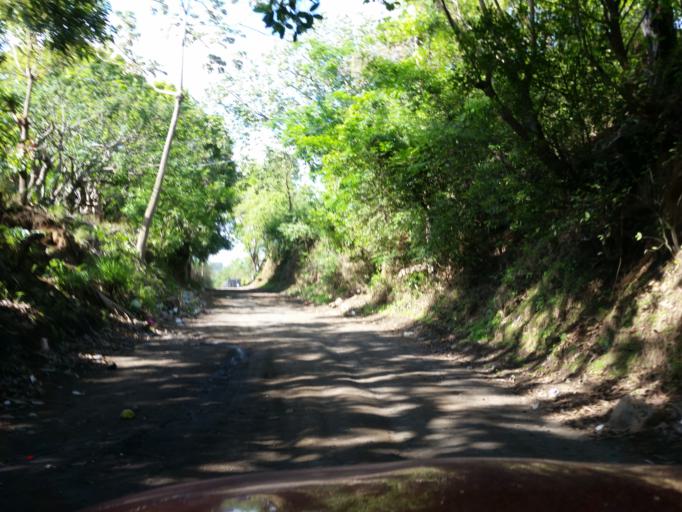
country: NI
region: Managua
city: Managua
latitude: 12.0868
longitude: -86.2620
